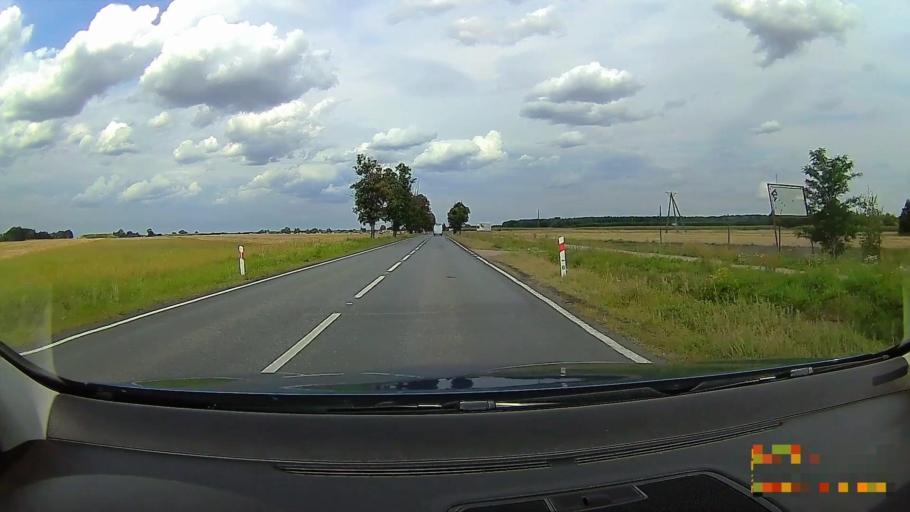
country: PL
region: Greater Poland Voivodeship
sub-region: Powiat koninski
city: Rychwal
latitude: 52.0822
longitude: 18.1617
